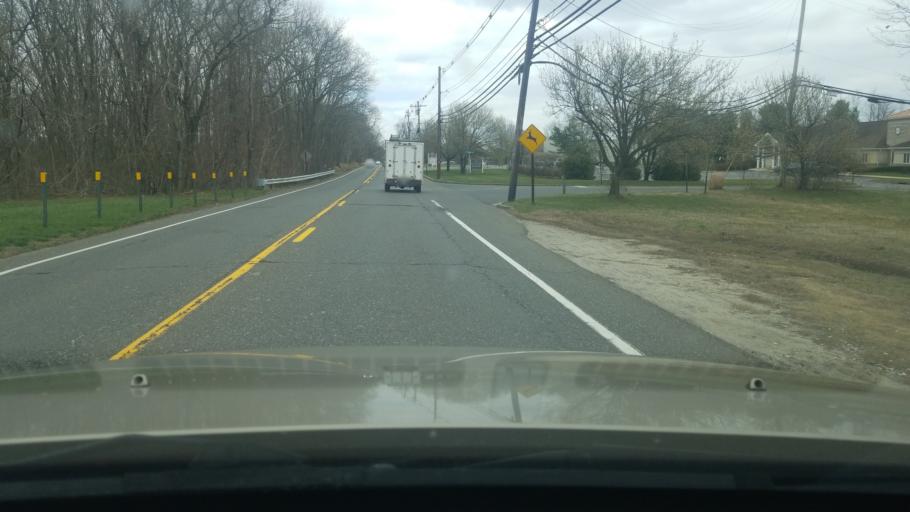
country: US
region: New Jersey
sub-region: Monmouth County
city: Manasquan
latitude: 40.1402
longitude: -74.0888
